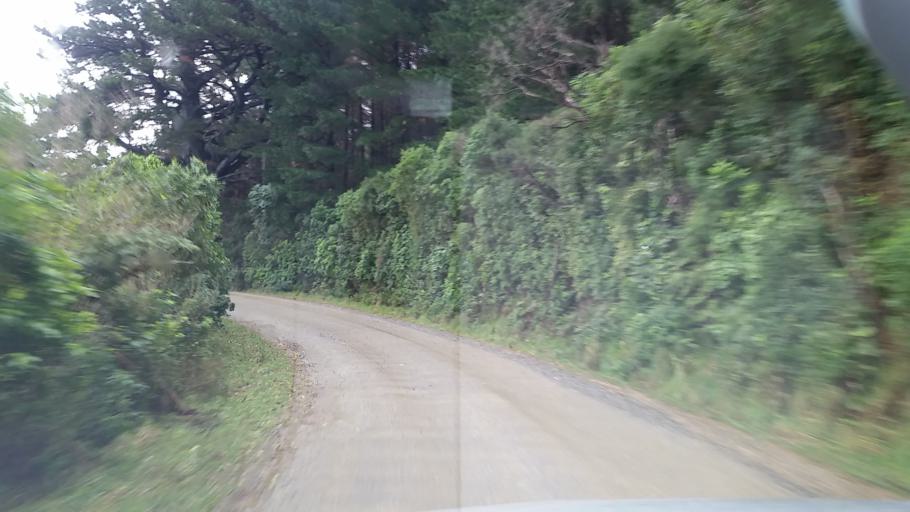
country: NZ
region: Marlborough
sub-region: Marlborough District
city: Picton
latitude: -41.1751
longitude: 174.0432
